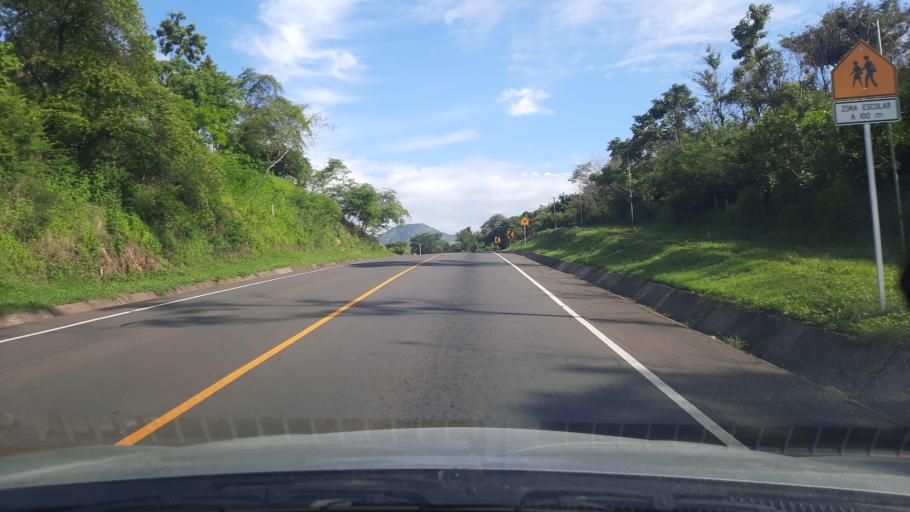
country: NI
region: Leon
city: Telica
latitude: 12.6881
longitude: -86.8507
